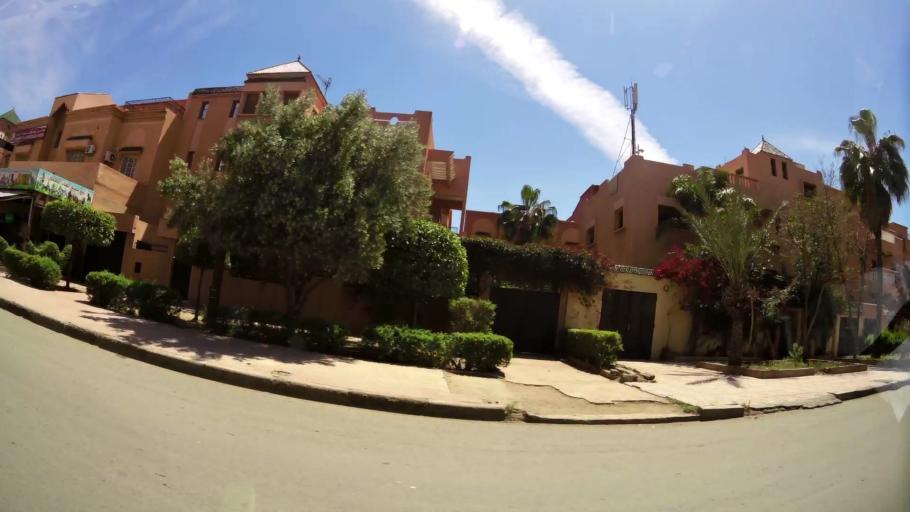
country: MA
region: Marrakech-Tensift-Al Haouz
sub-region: Marrakech
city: Marrakesh
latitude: 31.6385
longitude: -8.0615
